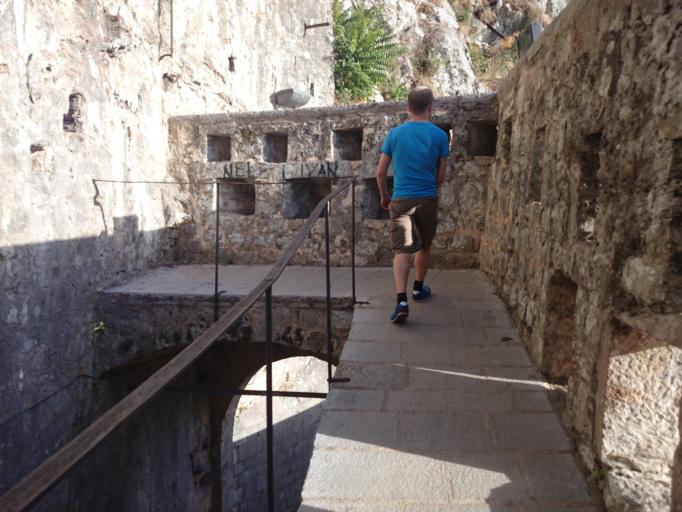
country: ME
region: Kotor
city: Kotor
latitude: 42.4223
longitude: 18.7716
